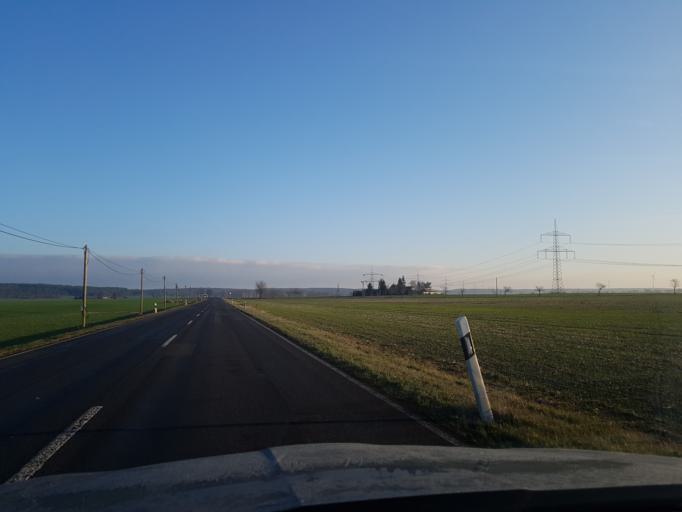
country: DE
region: Brandenburg
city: Schlieben
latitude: 51.7270
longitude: 13.4162
